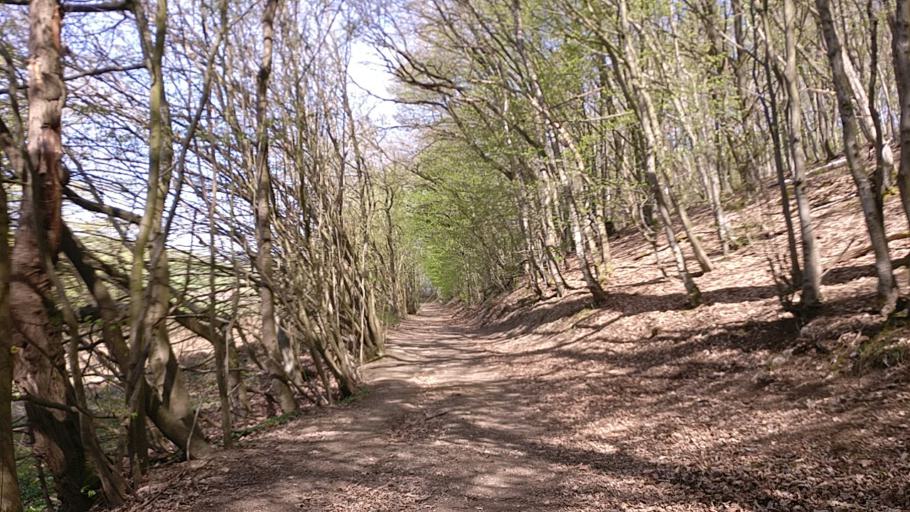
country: DE
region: Rheinland-Pfalz
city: Asbach
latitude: 50.6550
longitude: 7.4270
